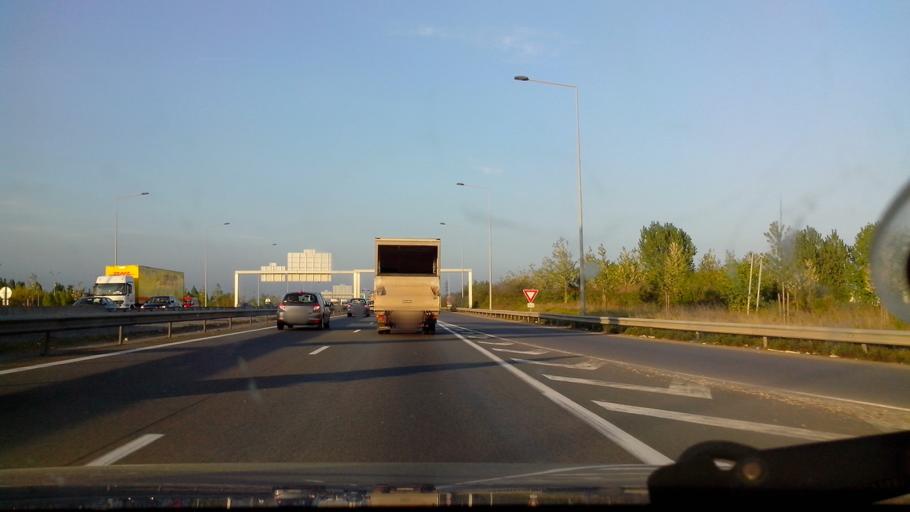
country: FR
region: Ile-de-France
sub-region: Departement de l'Essonne
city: Villabe
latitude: 48.6113
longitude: 2.4472
